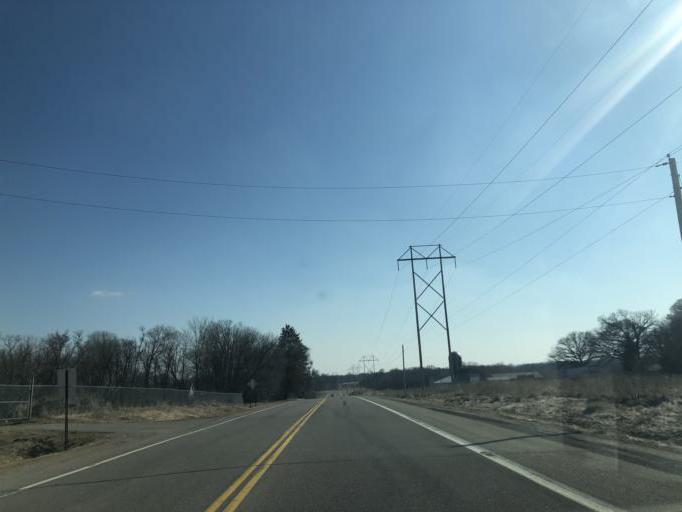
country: US
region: Minnesota
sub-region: Sherburne County
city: Becker
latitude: 45.4291
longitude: -93.8401
